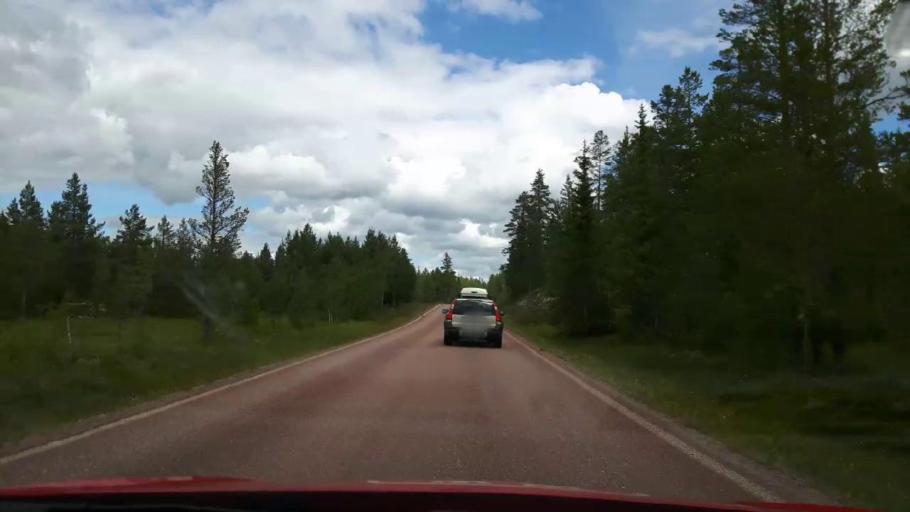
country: NO
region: Hedmark
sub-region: Trysil
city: Innbygda
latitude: 61.8975
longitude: 12.9878
